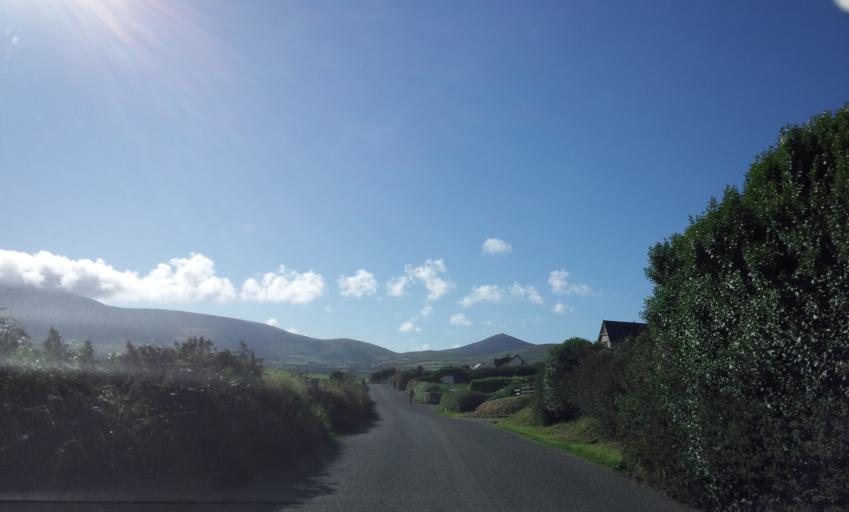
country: IE
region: Munster
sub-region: Ciarrai
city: Dingle
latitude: 52.1307
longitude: -10.3506
